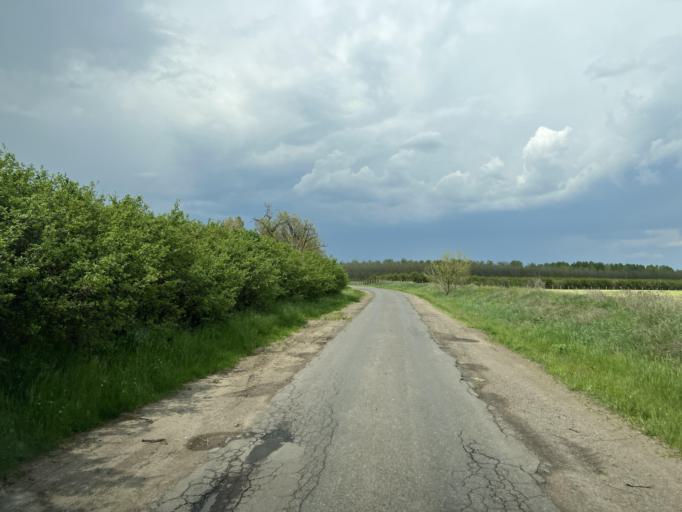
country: HU
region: Pest
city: Nagykoros
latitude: 46.9908
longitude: 19.8037
